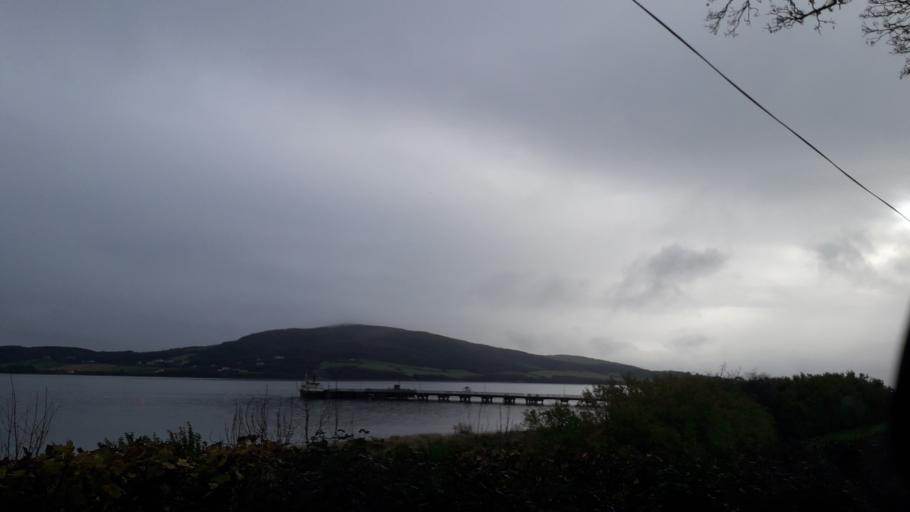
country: IE
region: Ulster
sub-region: County Donegal
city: Buncrana
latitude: 55.0975
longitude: -7.5306
